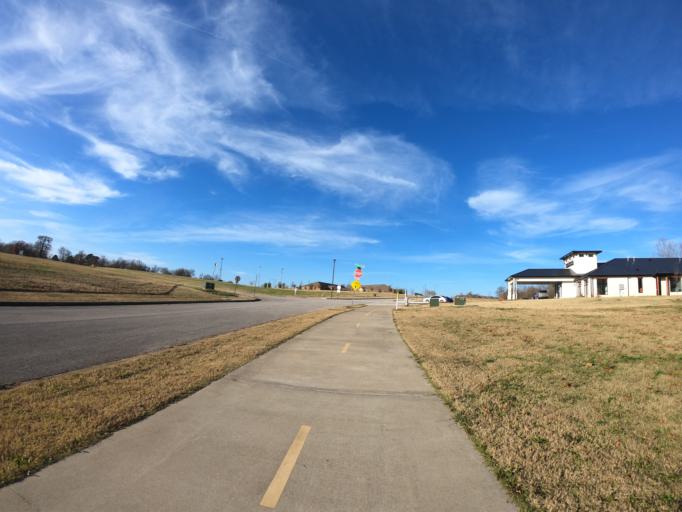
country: US
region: Arkansas
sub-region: Benton County
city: Rogers
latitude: 36.3235
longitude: -94.1761
